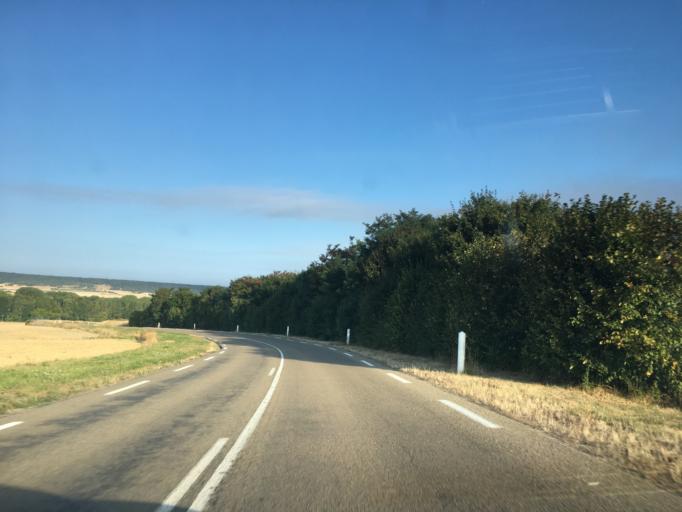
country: FR
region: Bourgogne
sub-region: Departement de l'Yonne
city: Aillant-sur-Tholon
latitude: 47.8601
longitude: 3.3653
